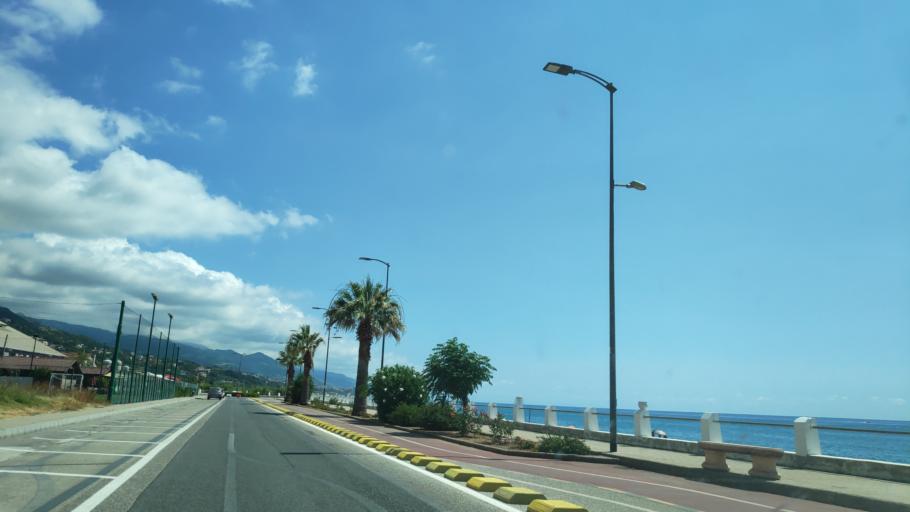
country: IT
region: Calabria
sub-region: Provincia di Cosenza
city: Paola
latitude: 39.3551
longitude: 16.0336
